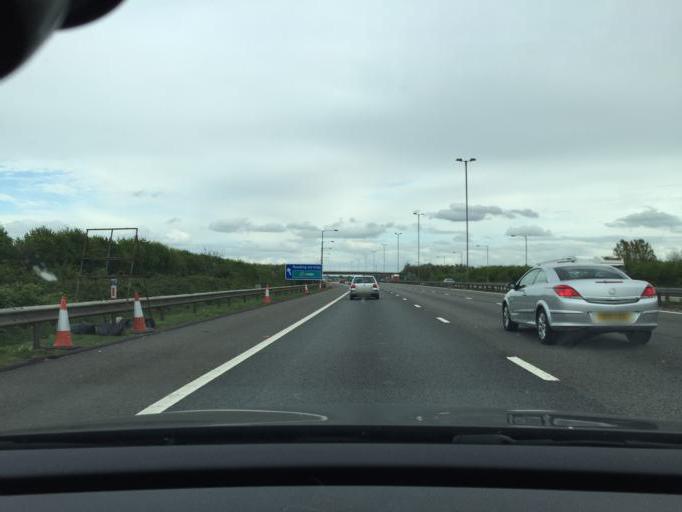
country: GB
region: England
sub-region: West Berkshire
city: Calcot
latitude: 51.4254
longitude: -1.0372
